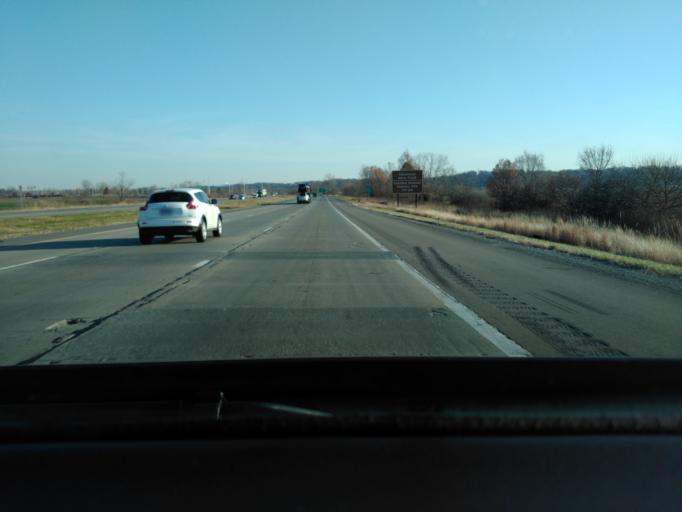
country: US
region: Illinois
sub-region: Saint Clair County
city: Caseyville
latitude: 38.6492
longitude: -90.0385
